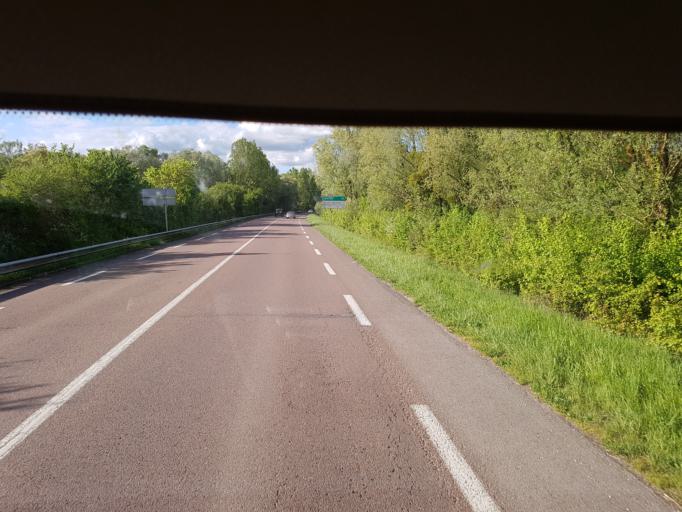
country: FR
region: Bourgogne
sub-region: Departement de l'Yonne
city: Saint-Florentin
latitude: 47.9983
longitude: 3.7354
